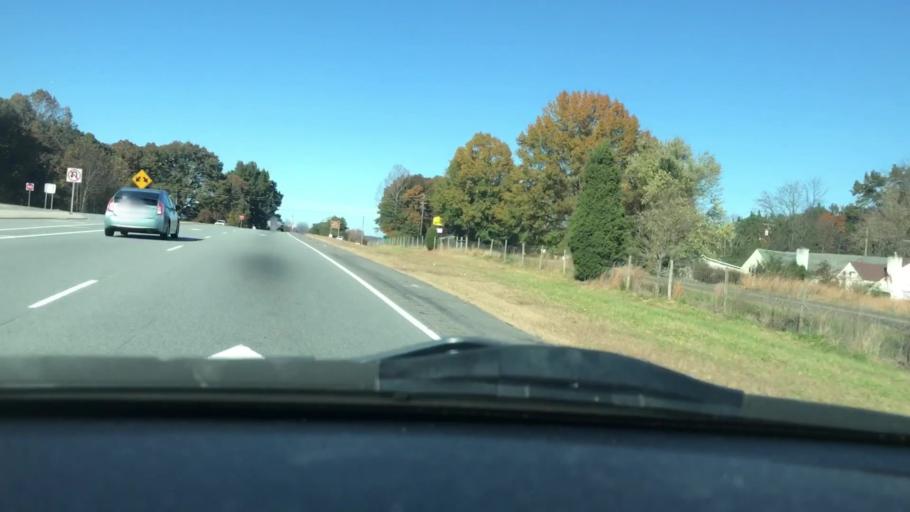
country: US
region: North Carolina
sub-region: Rockingham County
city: Madison
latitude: 36.3686
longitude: -79.9441
